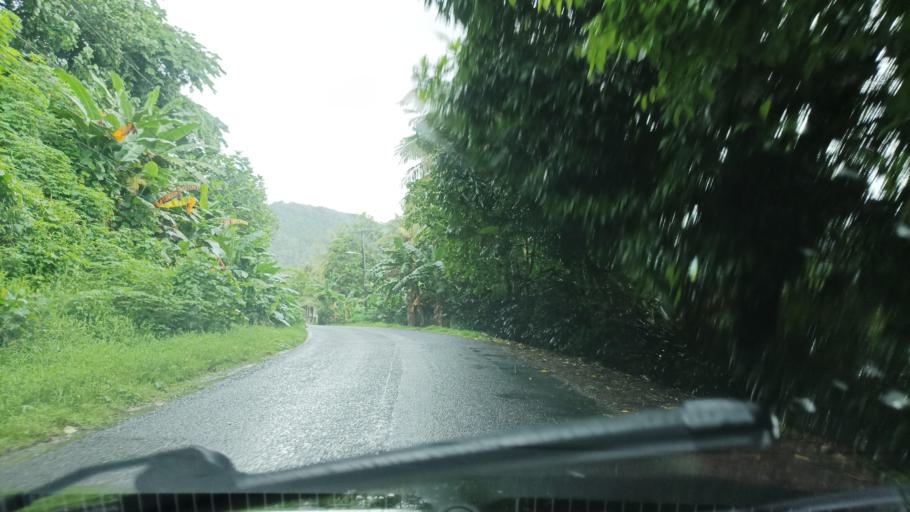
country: FM
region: Pohnpei
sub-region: Kolonia Municipality
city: Kolonia
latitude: 6.9534
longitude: 158.2289
